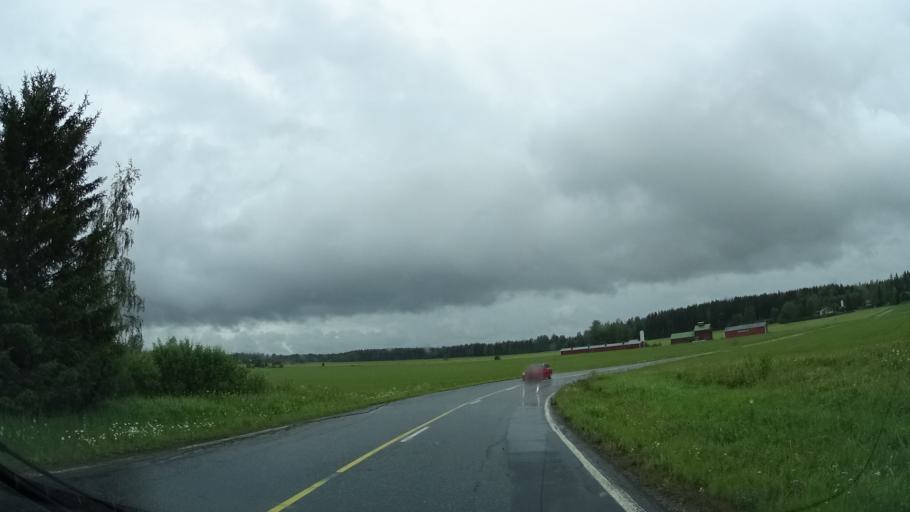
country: FI
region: Haeme
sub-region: Forssa
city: Humppila
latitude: 61.0007
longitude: 23.2523
